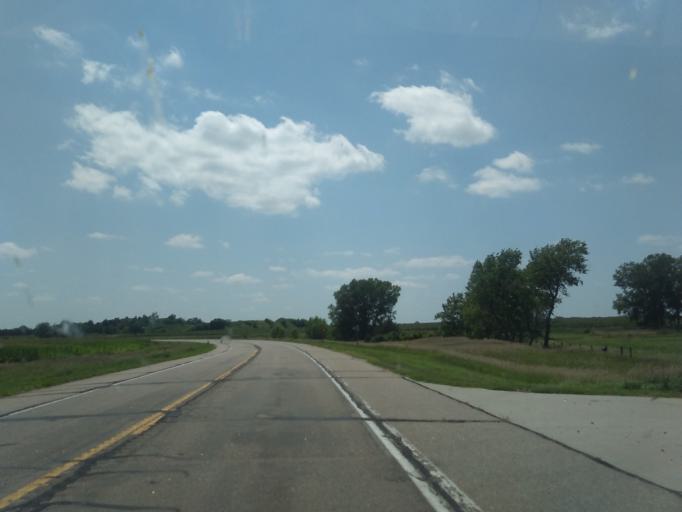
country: US
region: Nebraska
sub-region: Dawson County
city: Lexington
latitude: 40.6983
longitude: -99.7921
